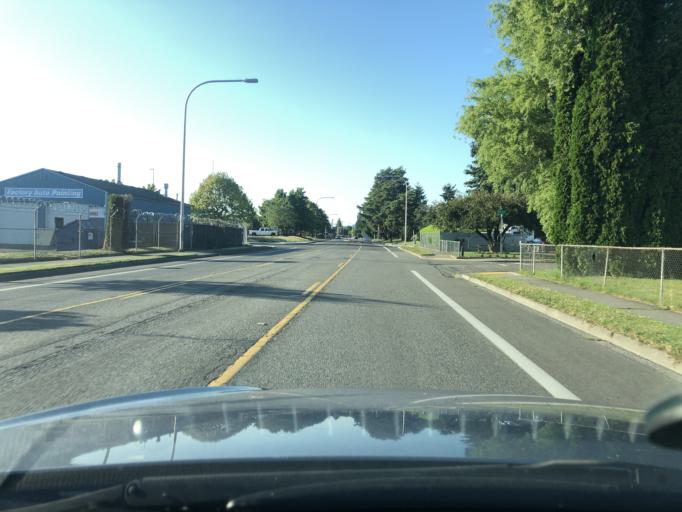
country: US
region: Washington
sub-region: King County
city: Auburn
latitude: 47.3225
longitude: -122.2191
